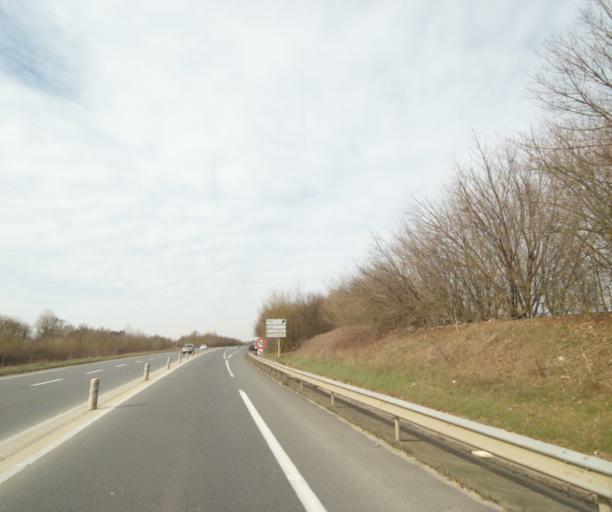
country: FR
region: Poitou-Charentes
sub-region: Departement des Deux-Sevres
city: Niort
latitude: 46.2941
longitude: -0.4531
